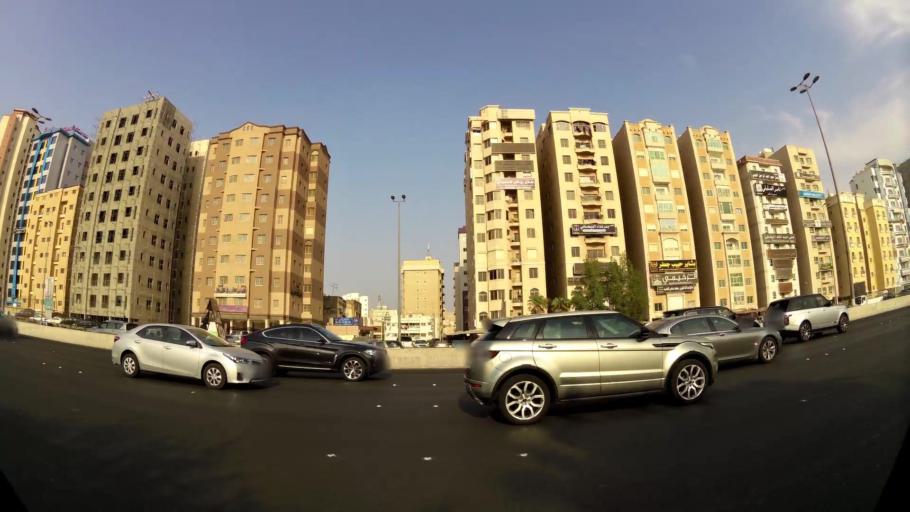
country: KW
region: Muhafazat Hawalli
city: Hawalli
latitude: 29.3293
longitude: 48.0078
